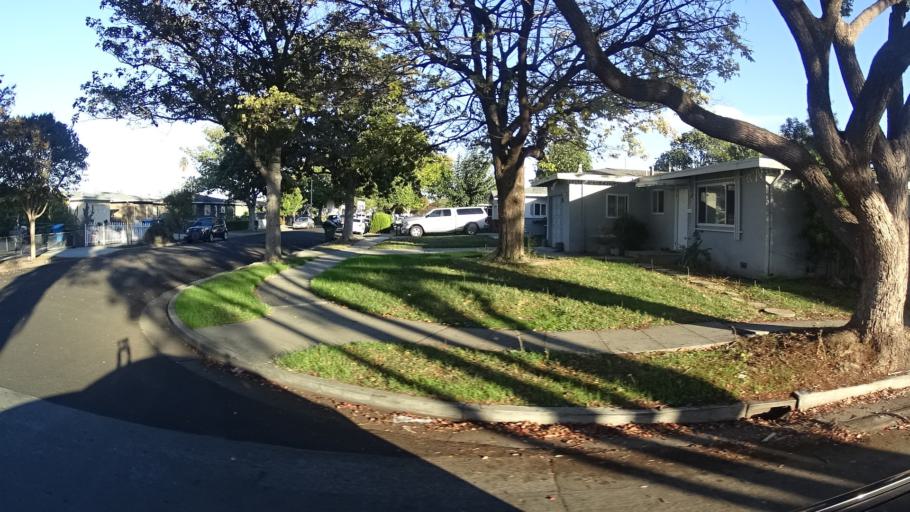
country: US
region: California
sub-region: Santa Clara County
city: Santa Clara
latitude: 37.3688
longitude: -121.9867
